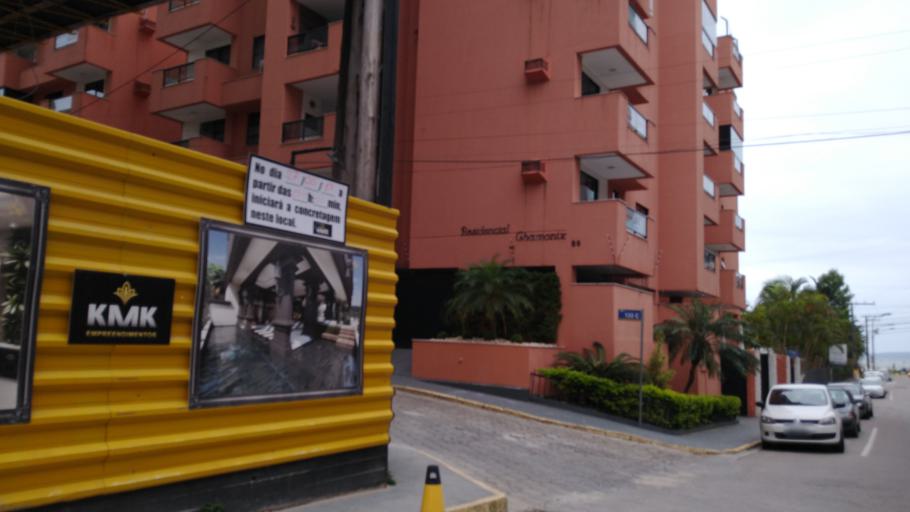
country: BR
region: Santa Catarina
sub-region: Itapema
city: Itapema
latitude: -27.0968
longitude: -48.6150
